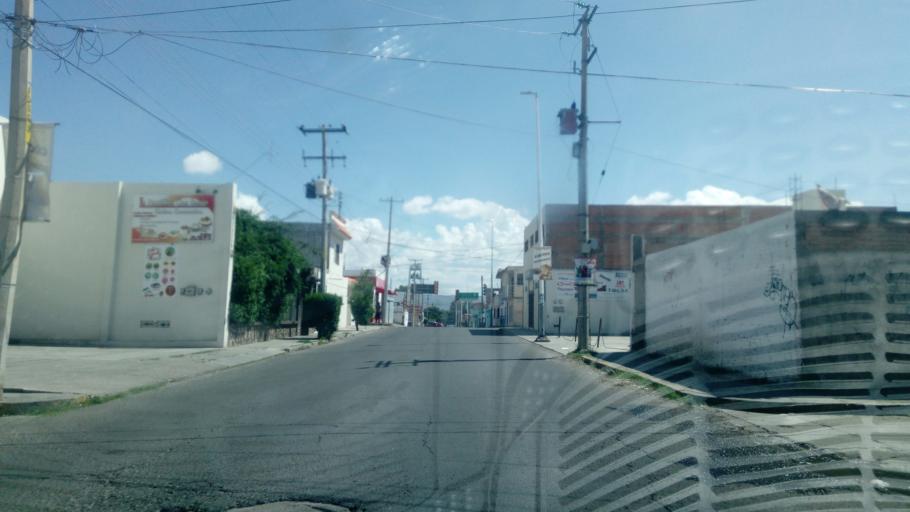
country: MX
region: Durango
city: Victoria de Durango
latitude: 24.0148
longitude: -104.6749
